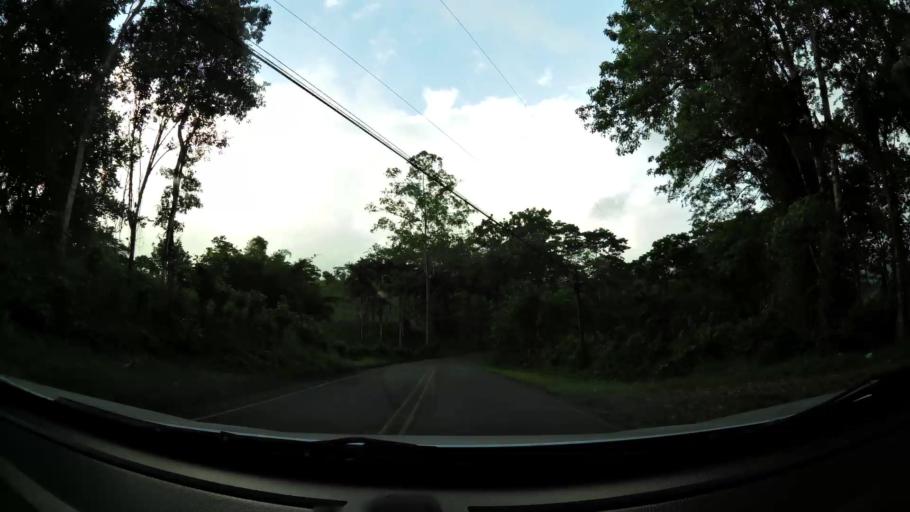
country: CR
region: Cartago
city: Turrialba
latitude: 9.9779
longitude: -83.5699
